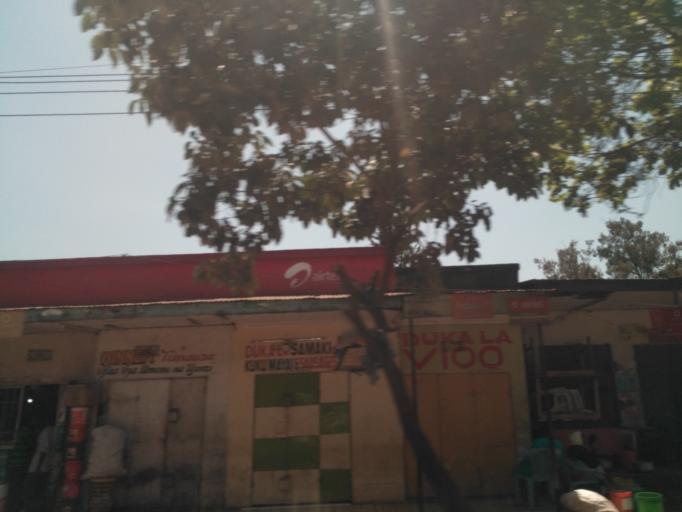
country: TZ
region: Arusha
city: Arusha
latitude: -3.3645
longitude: 36.6839
